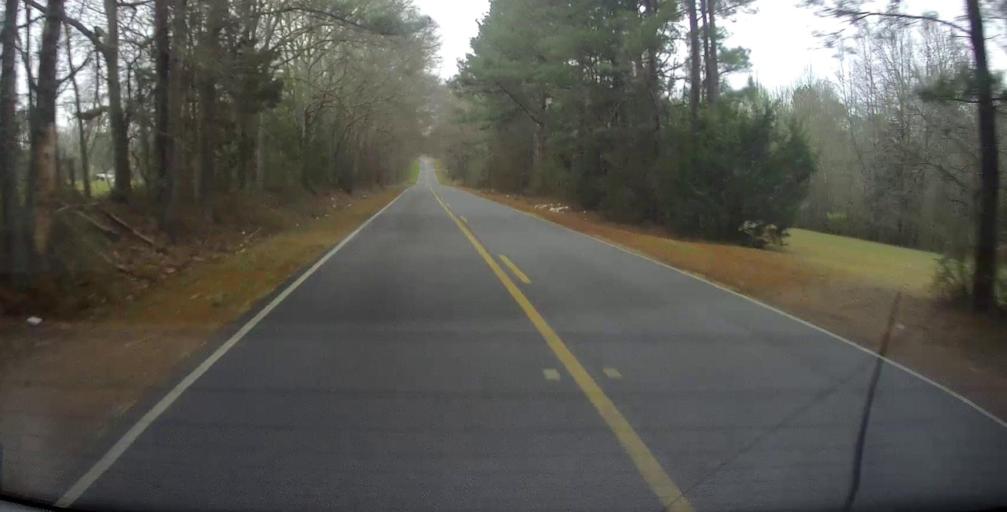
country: US
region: Georgia
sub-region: Pike County
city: Zebulon
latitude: 33.0622
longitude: -84.3254
